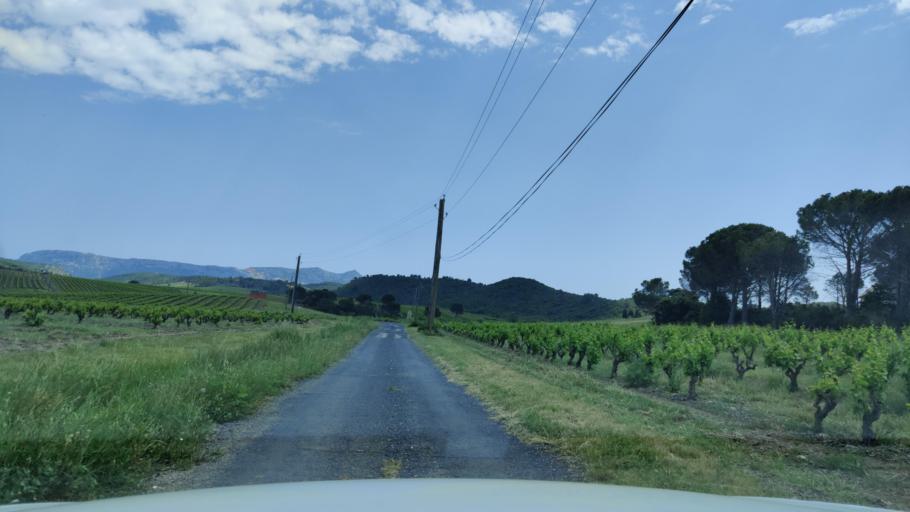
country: FR
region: Languedoc-Roussillon
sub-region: Departement des Pyrenees-Orientales
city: Estagel
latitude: 42.8147
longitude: 2.6789
